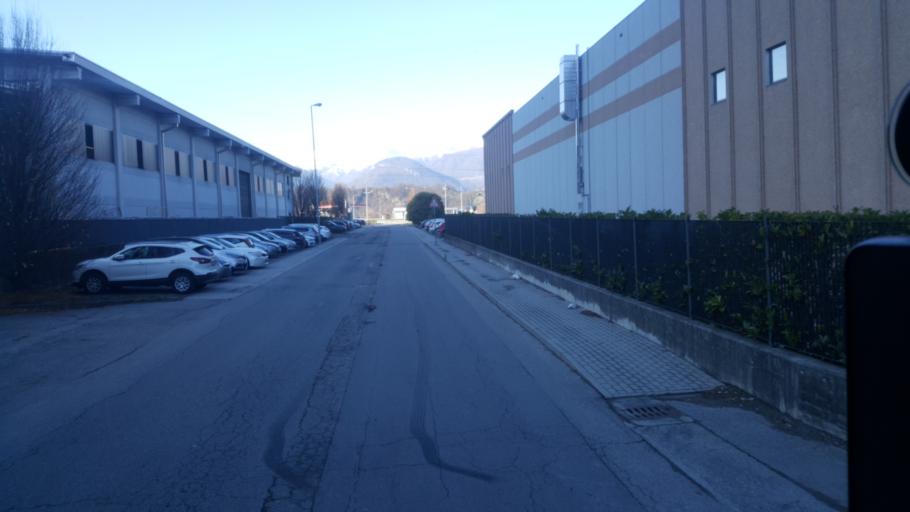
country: IT
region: Lombardy
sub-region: Provincia di Lecco
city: Colico Piano
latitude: 46.1411
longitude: 9.4014
